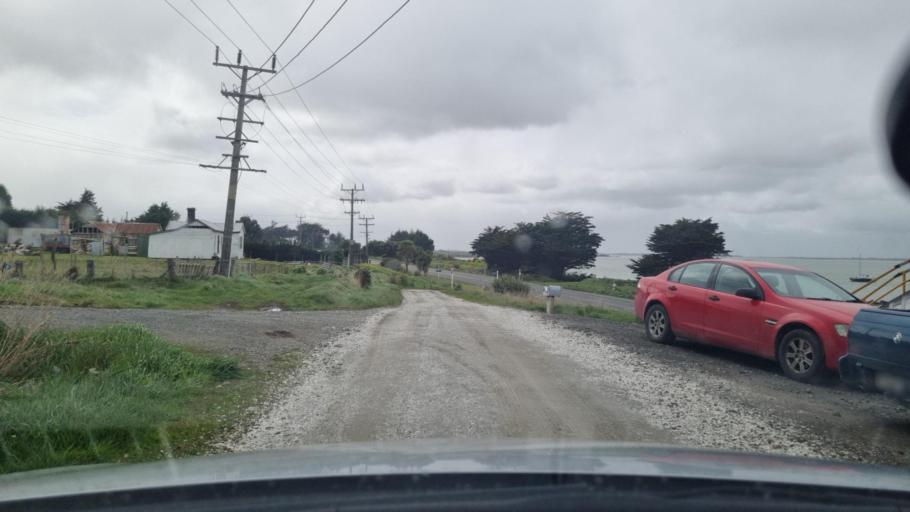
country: NZ
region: Southland
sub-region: Invercargill City
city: Bluff
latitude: -46.5849
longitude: 168.3043
